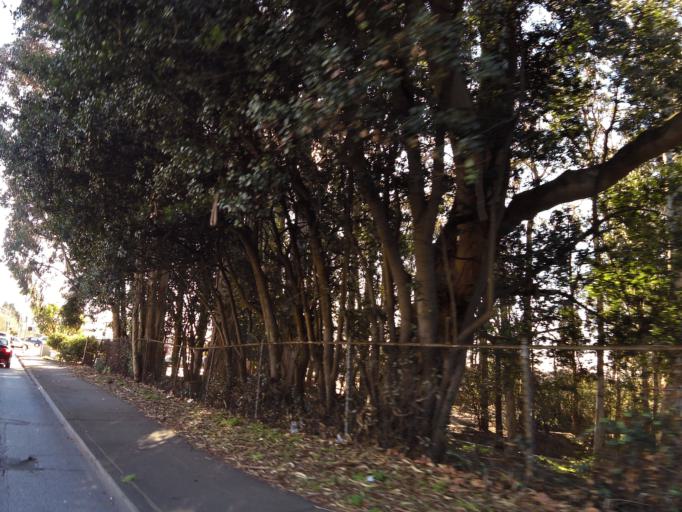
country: US
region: California
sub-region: San Mateo County
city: Daly City
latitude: 37.7354
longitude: -122.4753
